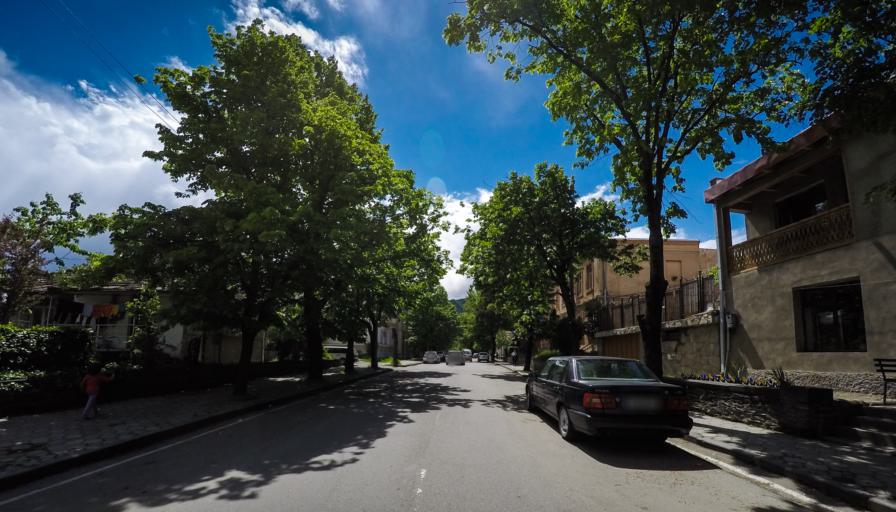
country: GE
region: Mtskheta-Mtianeti
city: Mtskheta
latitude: 41.8442
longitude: 44.7193
